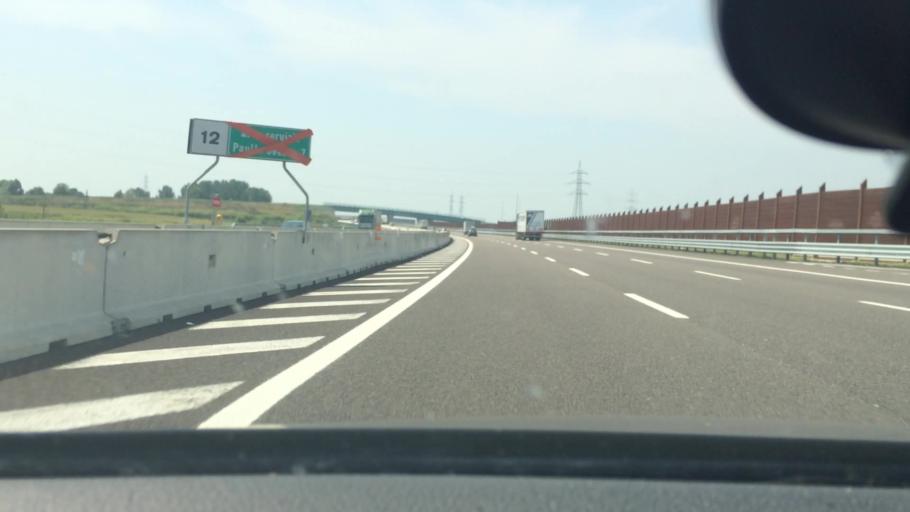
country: IT
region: Lombardy
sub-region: Citta metropolitana di Milano
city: Melzo
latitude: 45.4855
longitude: 9.4342
